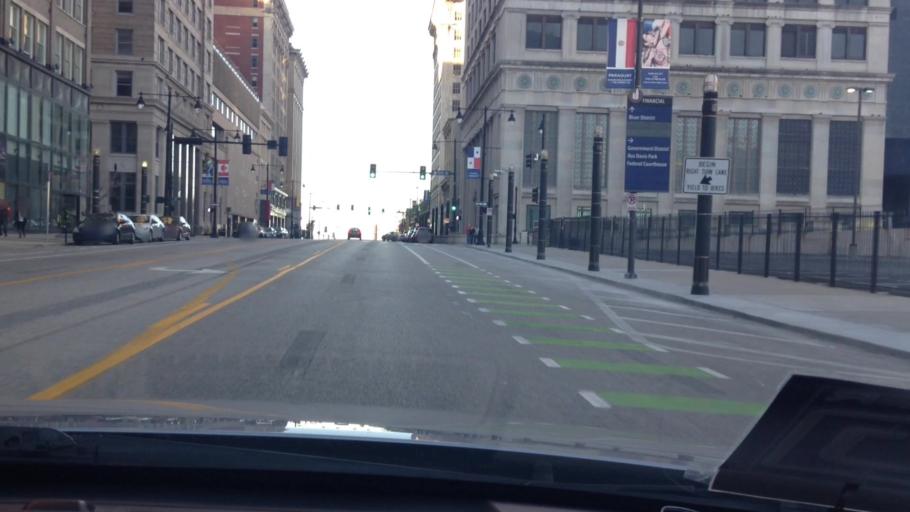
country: US
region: Missouri
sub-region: Jackson County
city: Kansas City
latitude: 39.1016
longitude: -94.5808
